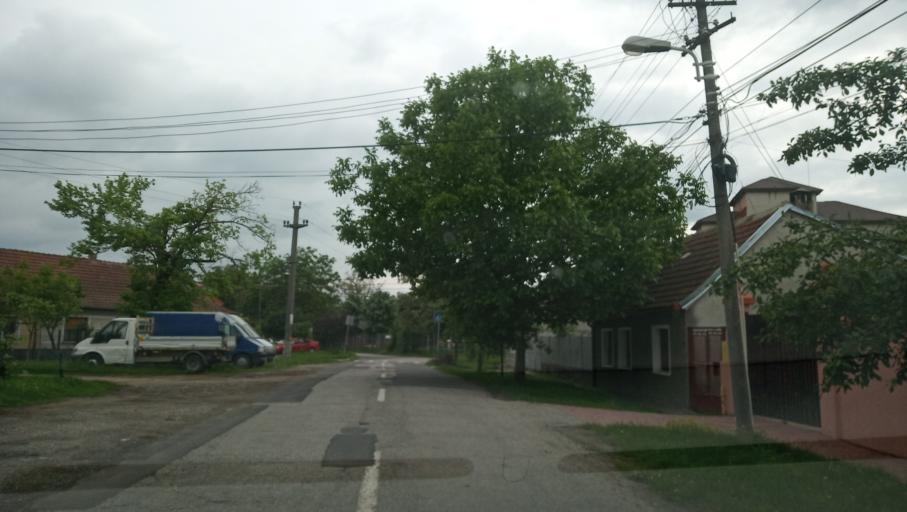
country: RO
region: Timis
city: Timisoara
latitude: 45.7536
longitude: 21.2627
